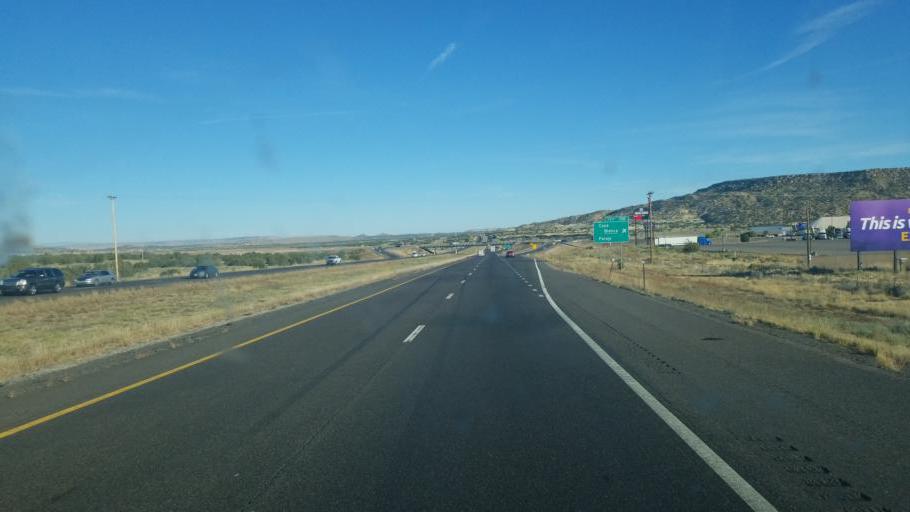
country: US
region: New Mexico
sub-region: Cibola County
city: Laguna
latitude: 35.0352
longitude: -107.4789
